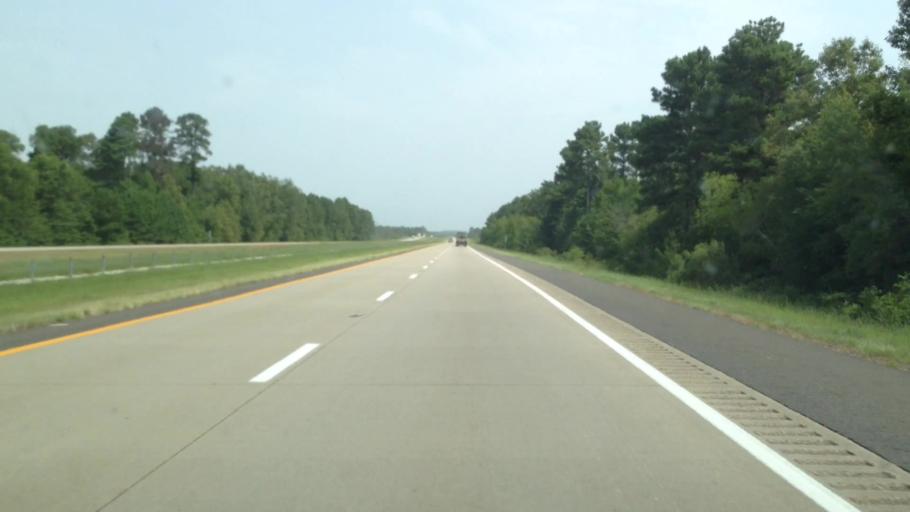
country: US
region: Texas
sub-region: Bowie County
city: Texarkana
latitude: 33.2157
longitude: -93.8735
